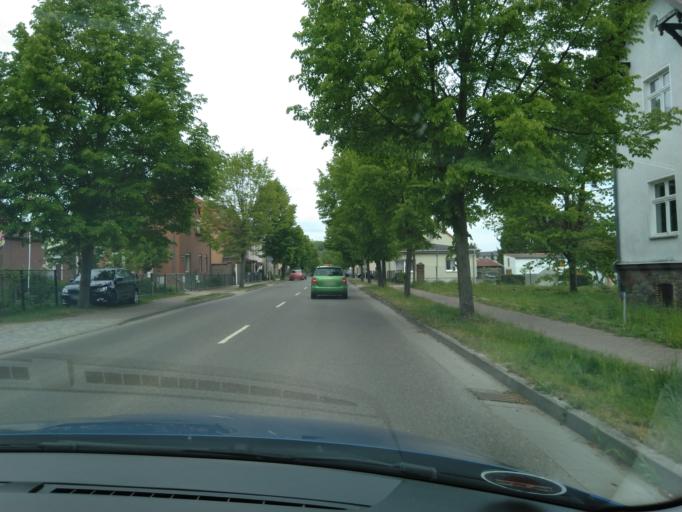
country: DE
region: Brandenburg
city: Oderberg
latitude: 52.8605
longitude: 14.0415
